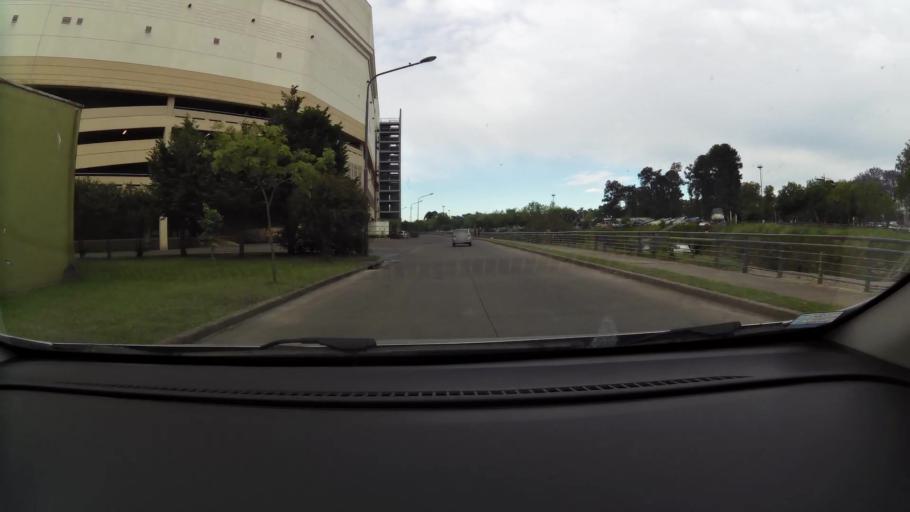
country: AR
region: Santa Fe
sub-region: Departamento de Rosario
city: Rosario
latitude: -32.9117
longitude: -60.6834
